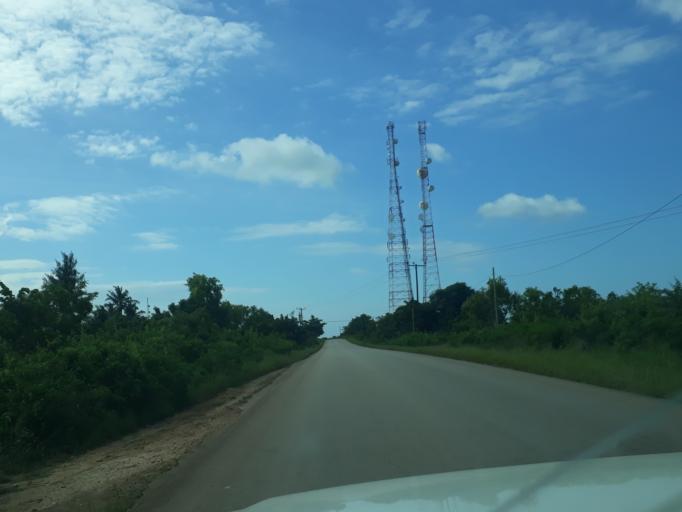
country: TZ
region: Zanzibar North
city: Nungwi
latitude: -5.7640
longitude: 39.3012
